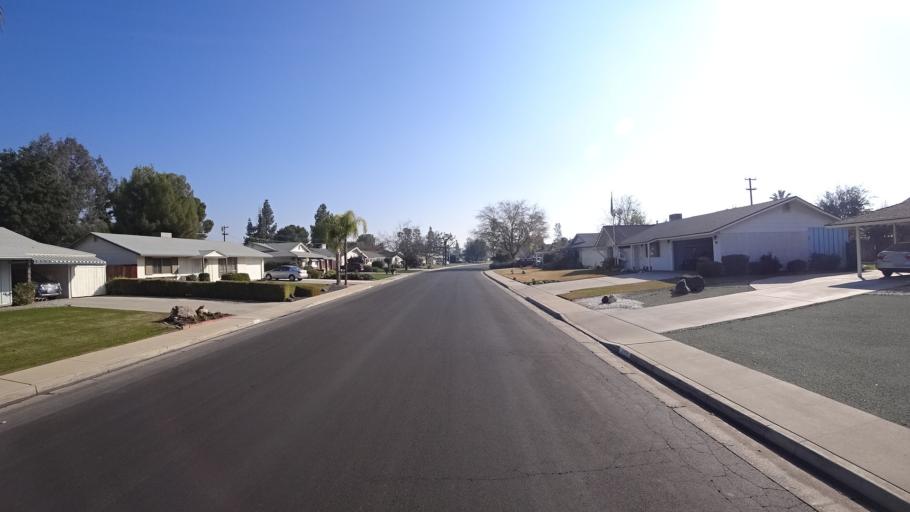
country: US
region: California
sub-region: Kern County
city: Bakersfield
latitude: 35.3510
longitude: -119.0662
